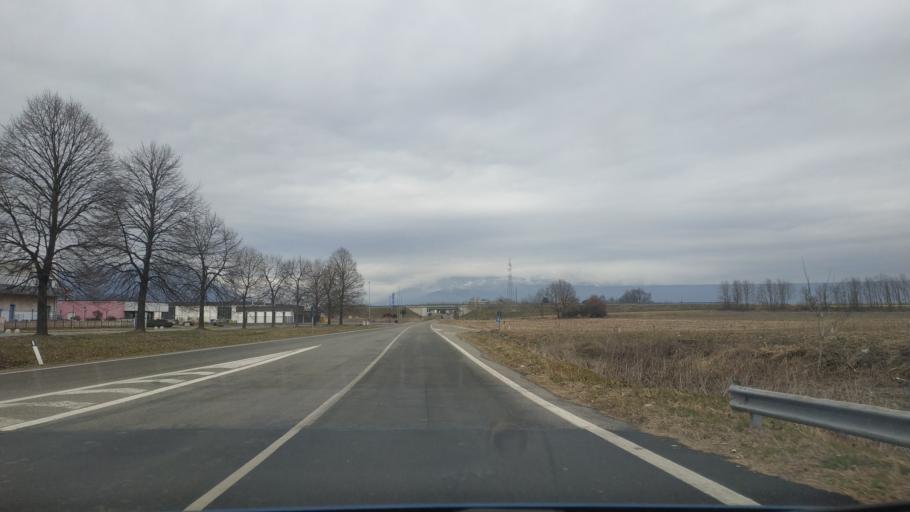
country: IT
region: Piedmont
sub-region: Provincia di Torino
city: Romano Canavese
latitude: 45.4180
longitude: 7.8833
